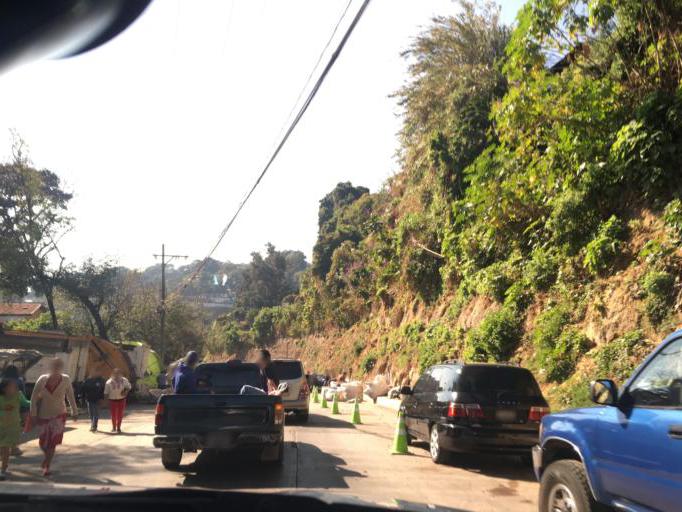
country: GT
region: Guatemala
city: Mixco
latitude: 14.6281
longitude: -90.6069
